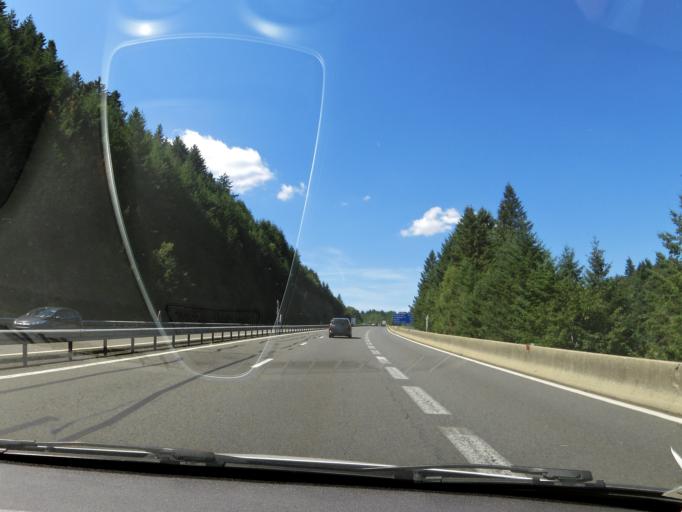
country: FR
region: Rhone-Alpes
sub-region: Departement de la Loire
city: Noiretable
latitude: 45.8509
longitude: 3.7801
